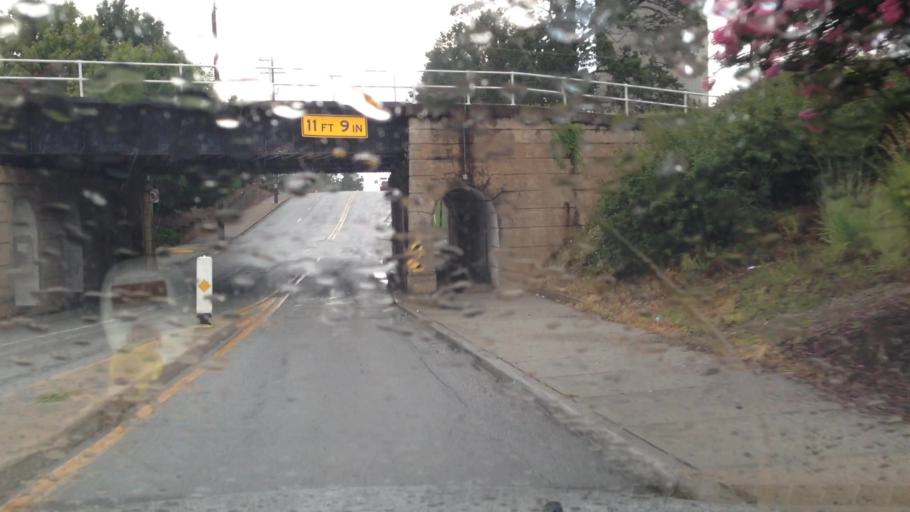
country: US
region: North Carolina
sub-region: Guilford County
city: Greensboro
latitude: 36.0628
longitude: -79.8154
